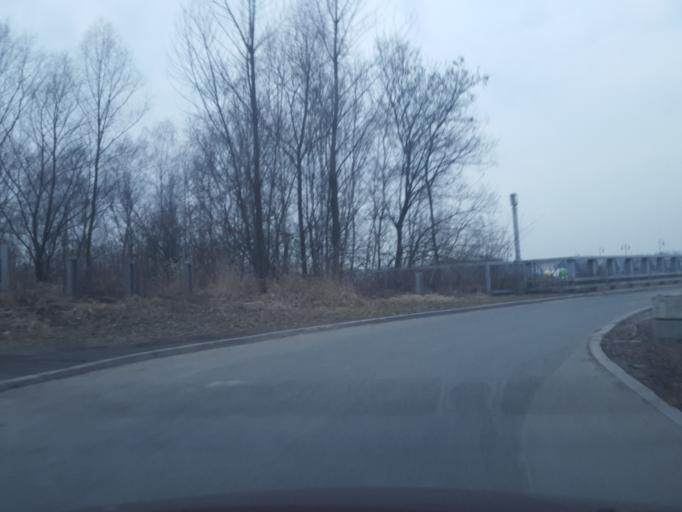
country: PL
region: Lesser Poland Voivodeship
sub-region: Krakow
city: Krakow
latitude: 50.0119
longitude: 19.9392
